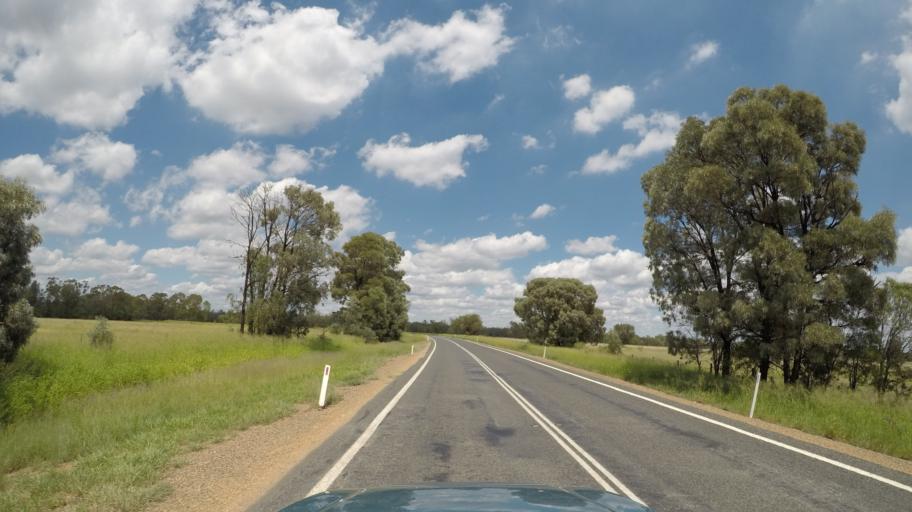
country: AU
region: Queensland
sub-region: Western Downs
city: Dalby
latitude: -27.9541
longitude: 151.1311
